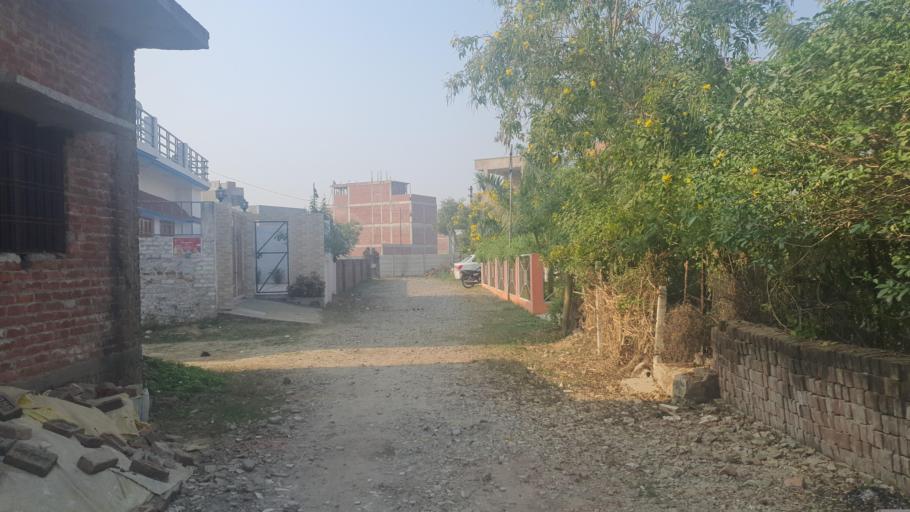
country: IN
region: Uttar Pradesh
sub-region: Lucknow District
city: Goshainganj
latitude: 26.7739
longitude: 81.0117
